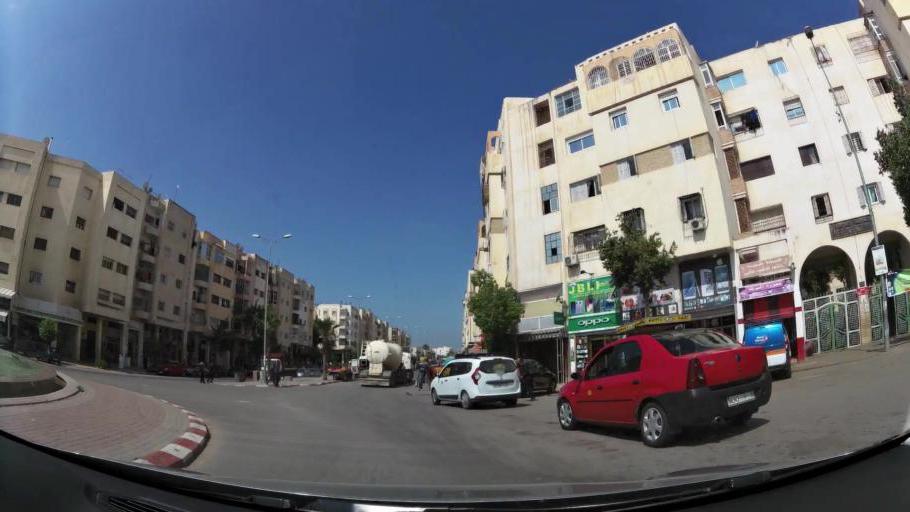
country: MA
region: Fes-Boulemane
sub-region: Fes
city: Fes
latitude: 34.0577
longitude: -5.0304
